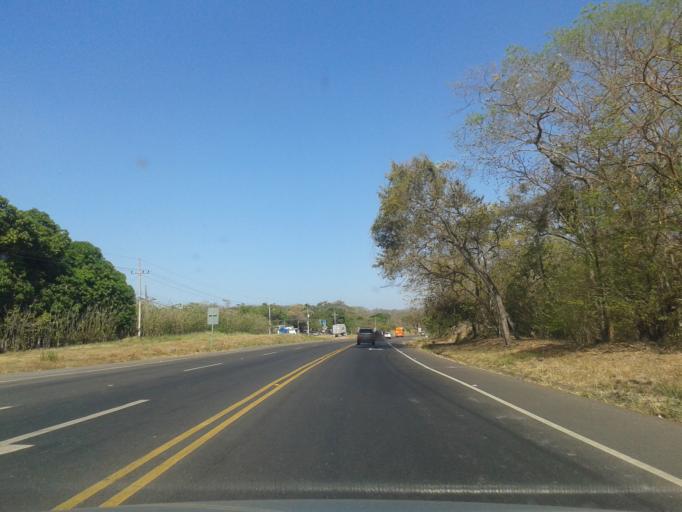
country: CR
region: Puntarenas
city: Esparza
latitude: 9.8947
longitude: -84.6529
